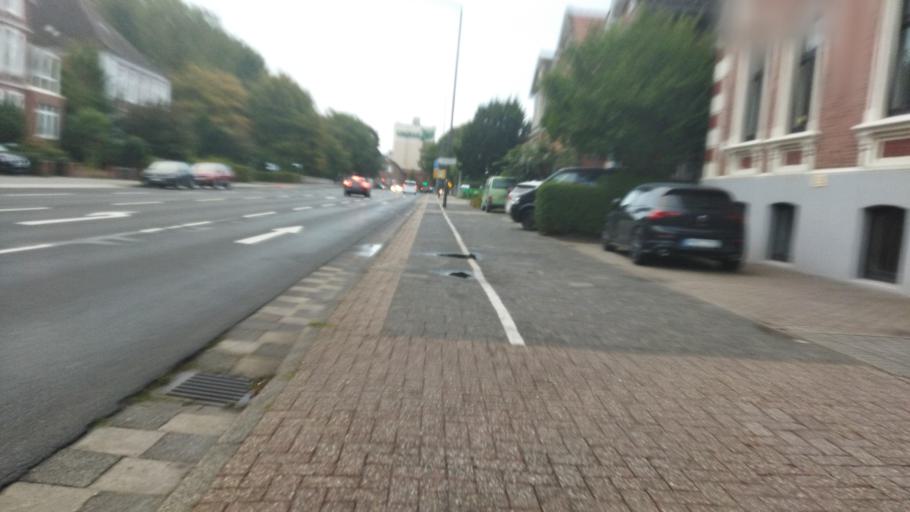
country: DE
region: Lower Saxony
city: Emden
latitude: 53.3751
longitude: 7.2071
